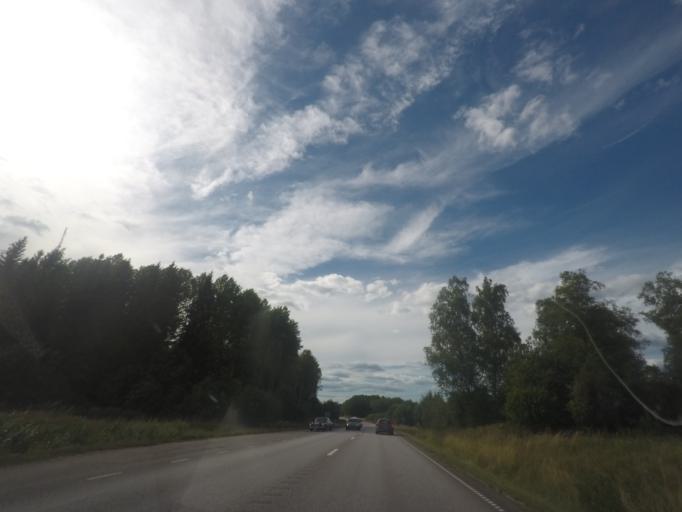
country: SE
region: Stockholm
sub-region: Norrtalje Kommun
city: Skanninge
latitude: 59.8987
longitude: 18.6090
